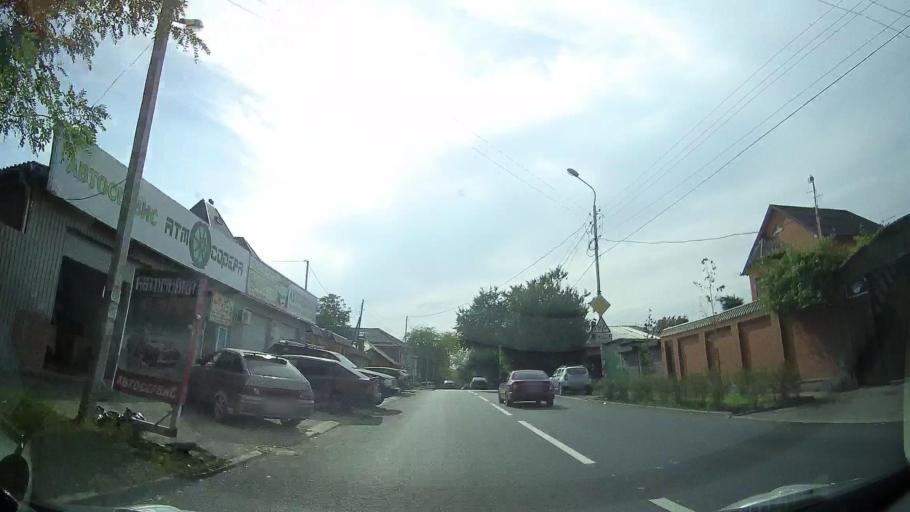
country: RU
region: Rostov
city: Rostov-na-Donu
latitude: 47.2545
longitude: 39.6959
